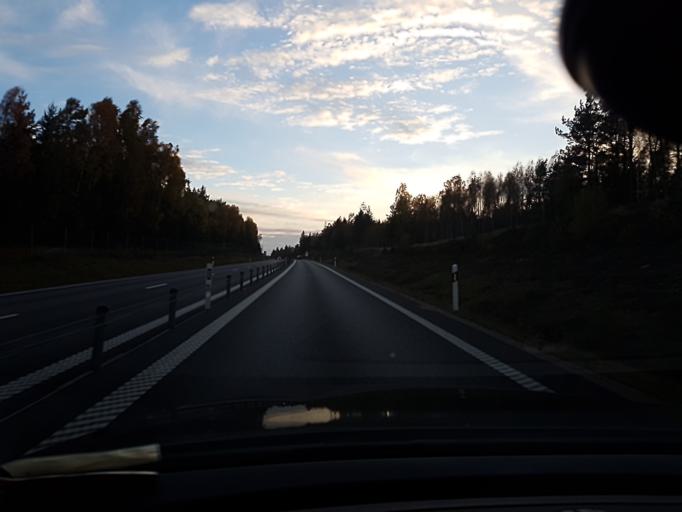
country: SE
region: Kronoberg
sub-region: Ljungby Kommun
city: Ljungby
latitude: 56.7841
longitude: 13.8246
